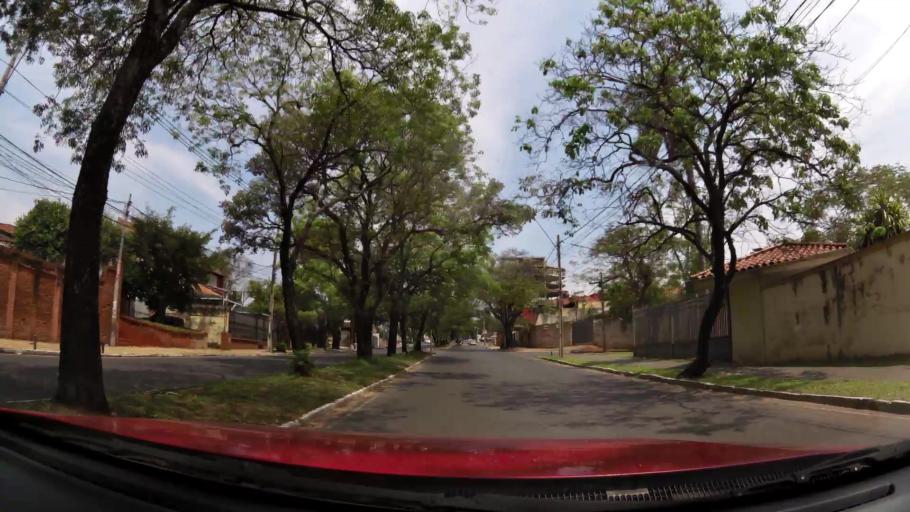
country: PY
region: Asuncion
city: Asuncion
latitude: -25.2802
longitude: -57.6003
